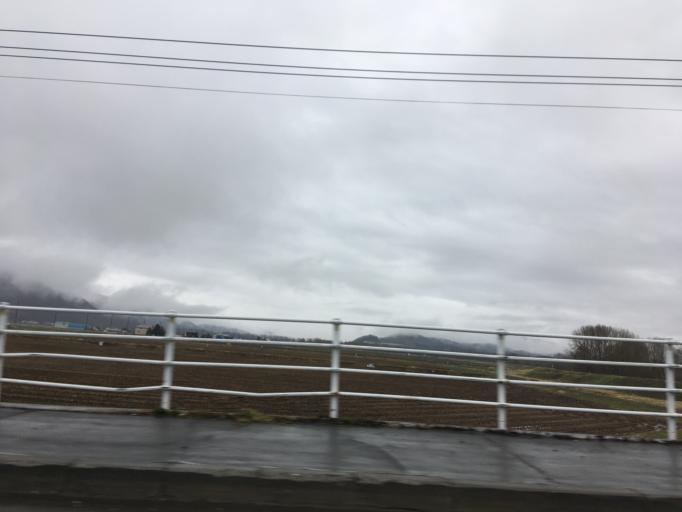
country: JP
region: Hokkaido
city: Nayoro
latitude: 44.1295
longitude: 142.4850
